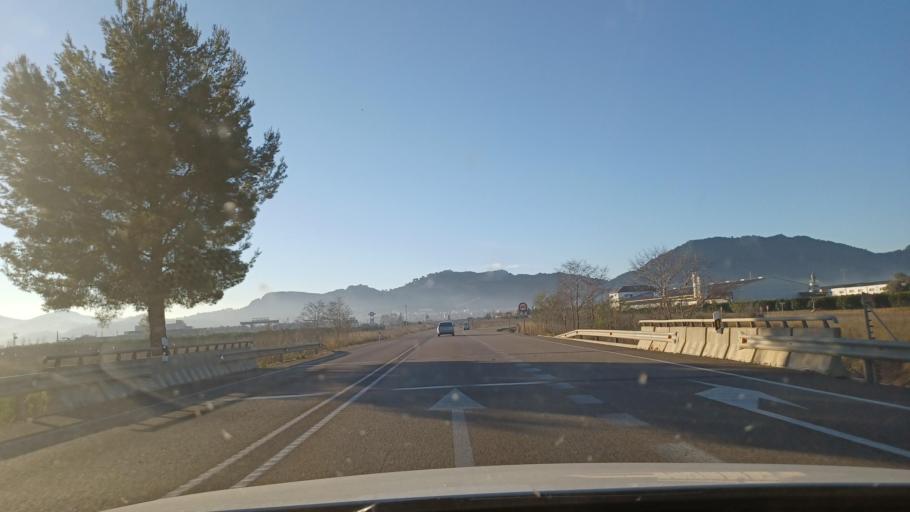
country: ES
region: Valencia
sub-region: Provincia de Valencia
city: Llosa de Ranes
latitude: 39.0094
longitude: -0.5323
